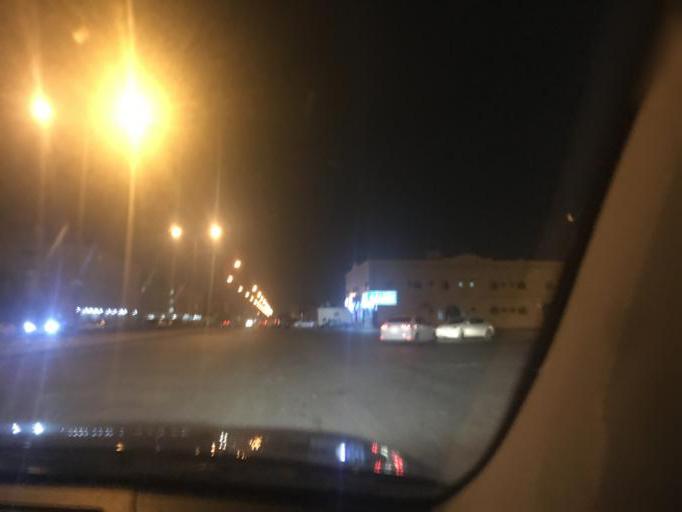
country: SA
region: Ar Riyad
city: Riyadh
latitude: 24.8226
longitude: 46.7409
